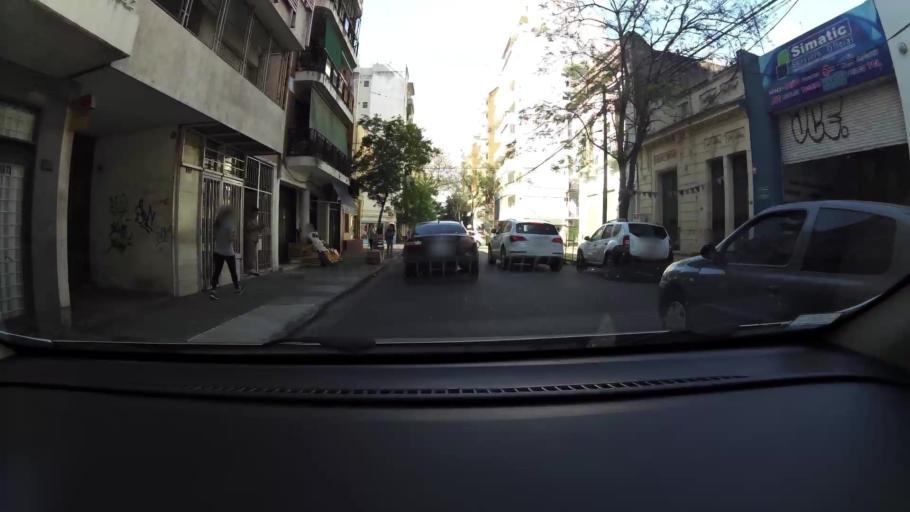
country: AR
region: Santa Fe
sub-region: Departamento de Rosario
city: Rosario
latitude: -32.9524
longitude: -60.6455
